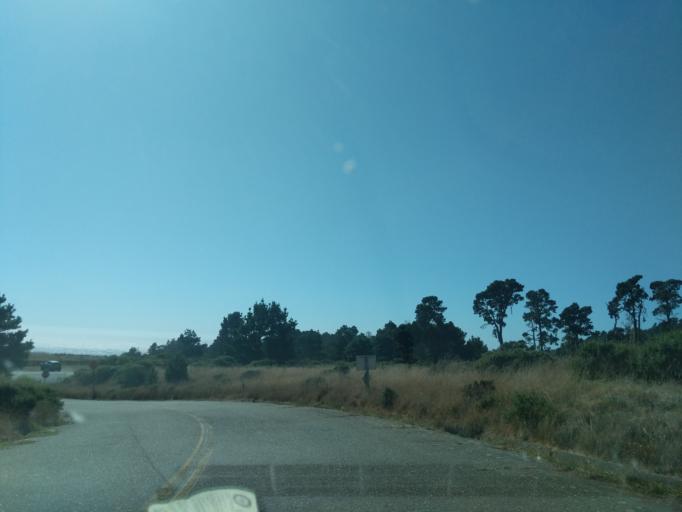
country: US
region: California
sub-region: Sonoma County
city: Monte Rio
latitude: 38.5192
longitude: -123.2460
